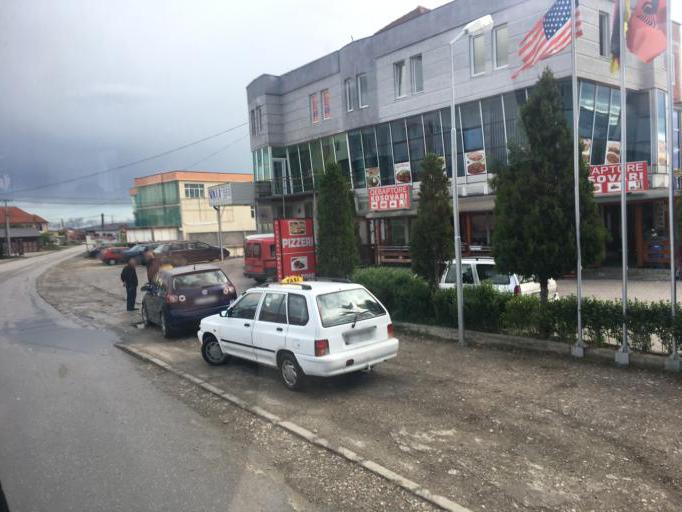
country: XK
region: Pristina
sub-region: Komuna e Drenasit
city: Glogovac
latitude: 42.5815
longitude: 20.8999
